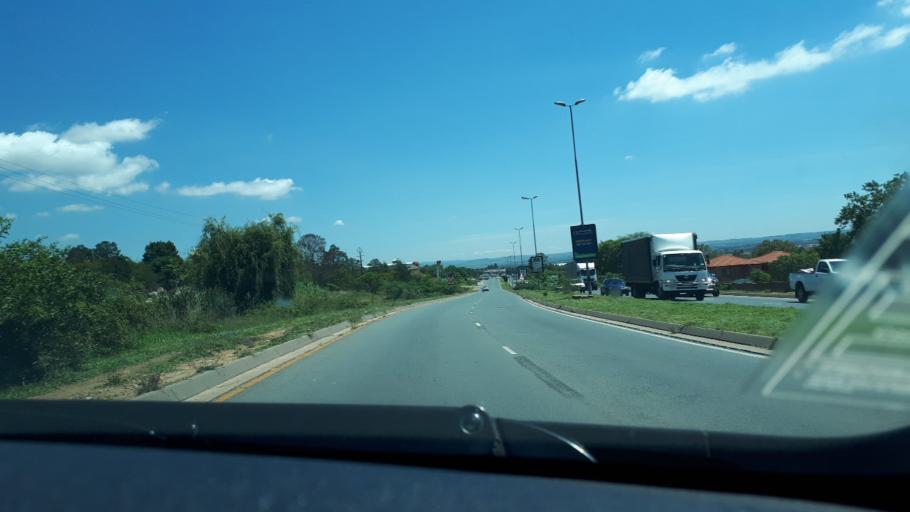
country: ZA
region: Gauteng
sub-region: West Rand District Municipality
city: Muldersdriseloop
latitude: -26.0587
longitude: 27.9547
